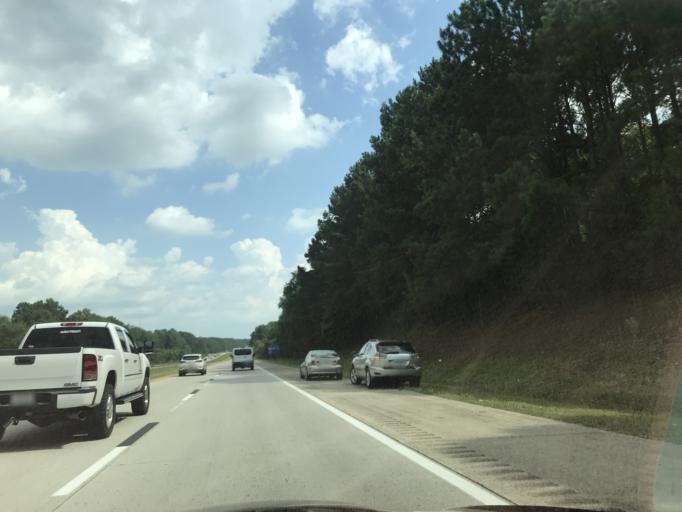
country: US
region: North Carolina
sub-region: Johnston County
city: Benson
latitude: 35.5238
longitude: -78.5630
